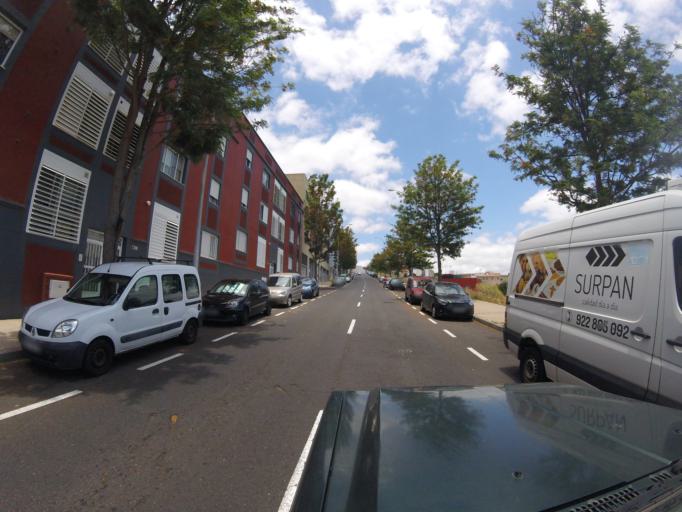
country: ES
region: Canary Islands
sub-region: Provincia de Santa Cruz de Tenerife
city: La Laguna
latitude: 28.4320
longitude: -16.3101
